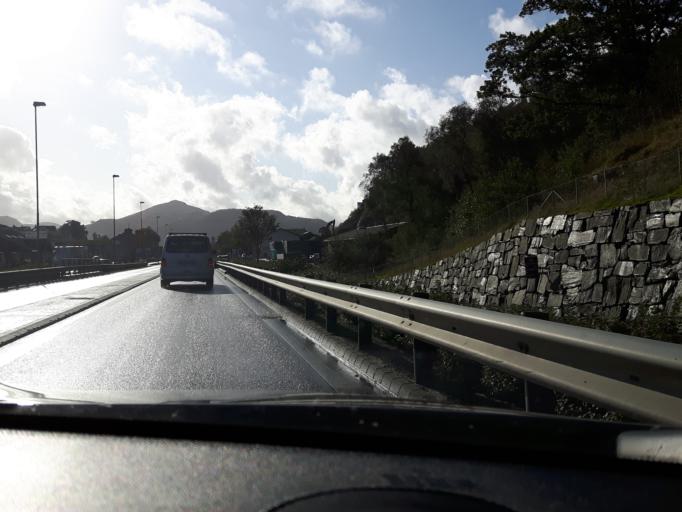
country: NO
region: Rogaland
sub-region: Gjesdal
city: Algard
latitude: 58.7688
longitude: 5.8578
